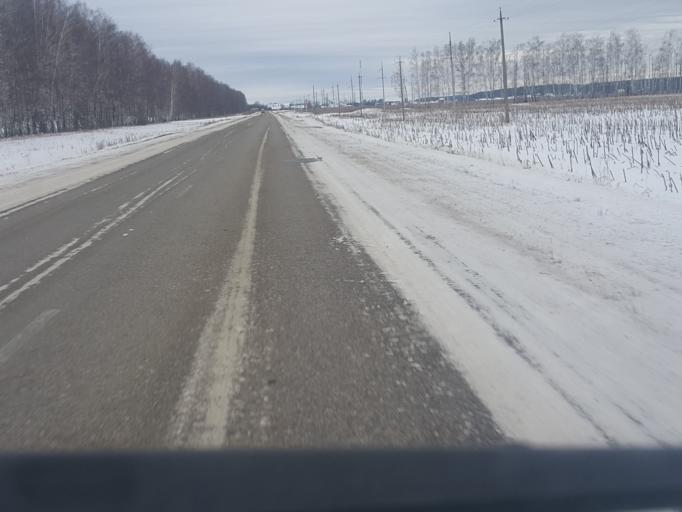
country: RU
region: Tambov
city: Rasskazovo
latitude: 52.8141
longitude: 41.7934
